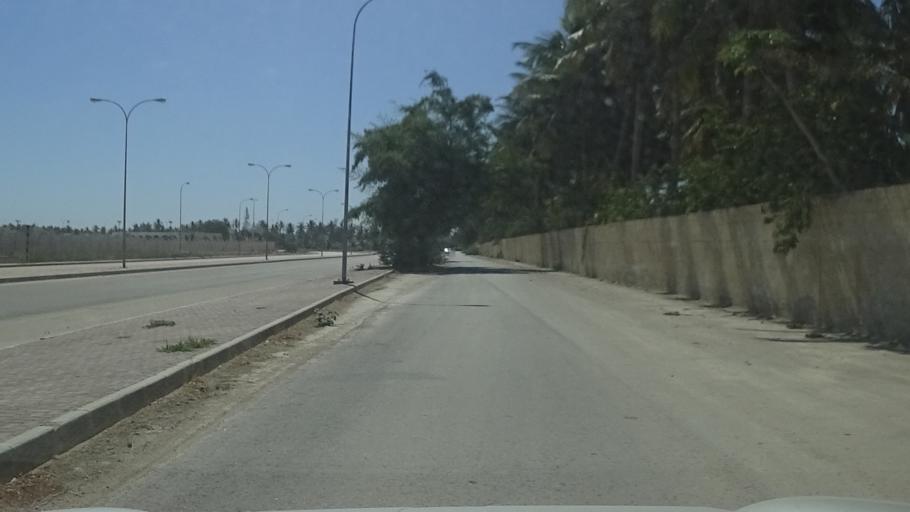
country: OM
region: Zufar
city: Salalah
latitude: 17.0289
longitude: 54.1229
